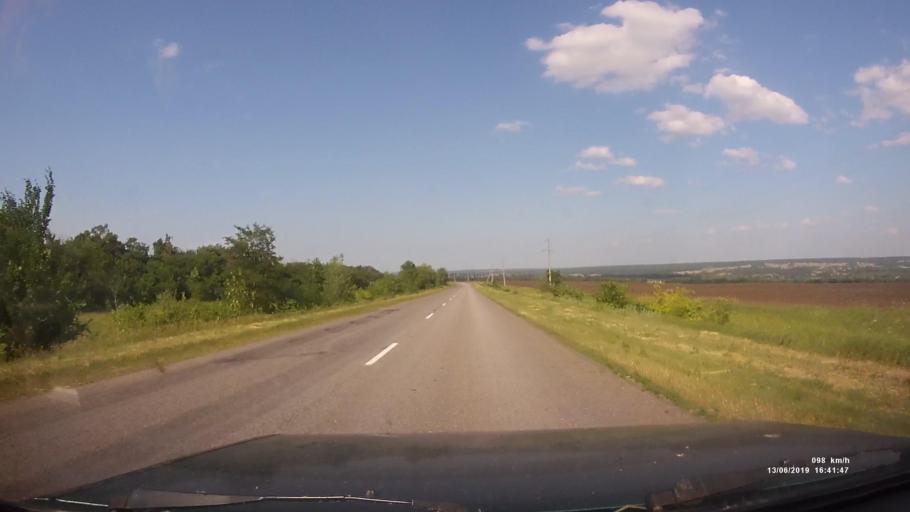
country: RU
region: Rostov
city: Kazanskaya
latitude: 49.9376
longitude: 41.3905
